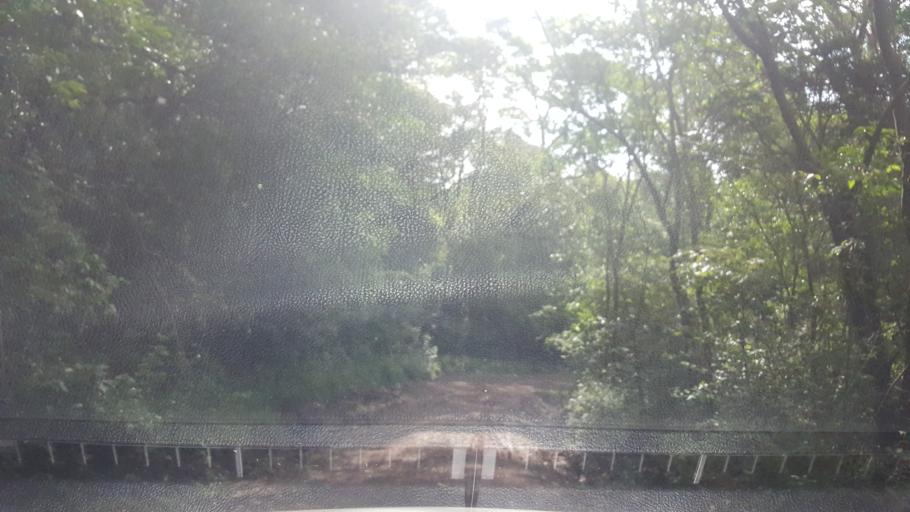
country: AR
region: Misiones
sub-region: Departamento de Candelaria
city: Candelaria
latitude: -27.5587
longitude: -55.7082
